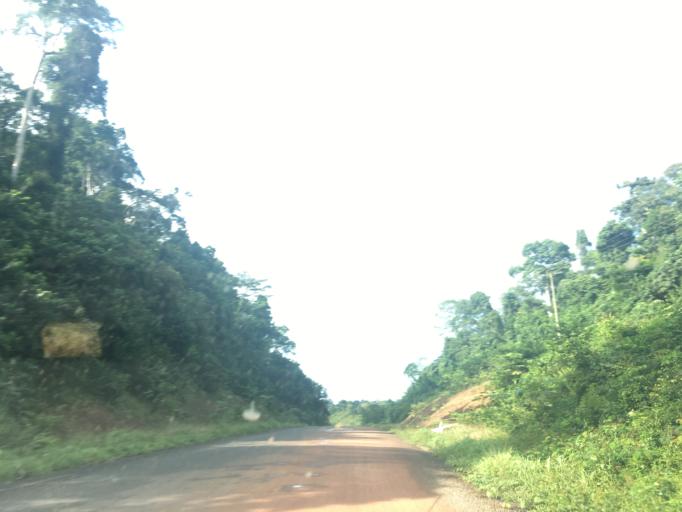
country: GH
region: Western
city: Wassa-Akropong
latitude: 5.9727
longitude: -2.4185
